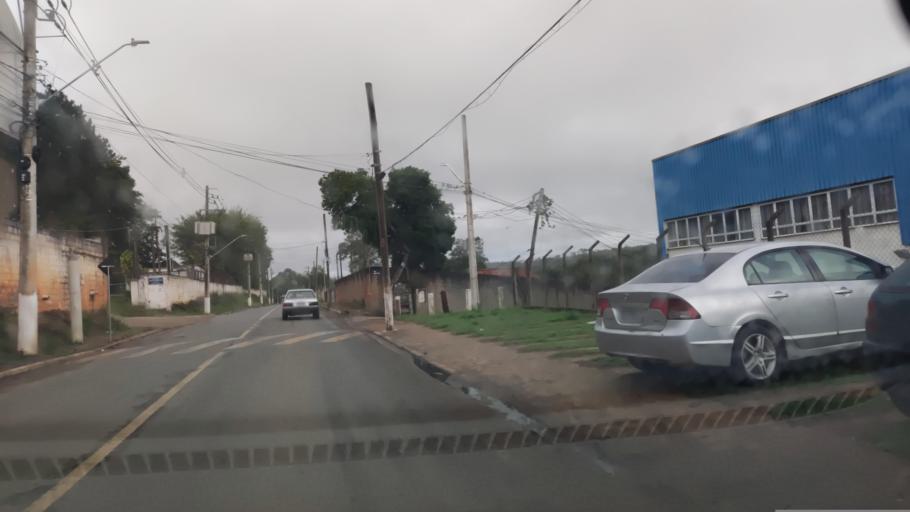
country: BR
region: Sao Paulo
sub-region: Vargem Grande Paulista
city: Vargem Grande Paulista
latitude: -23.6721
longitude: -47.0408
